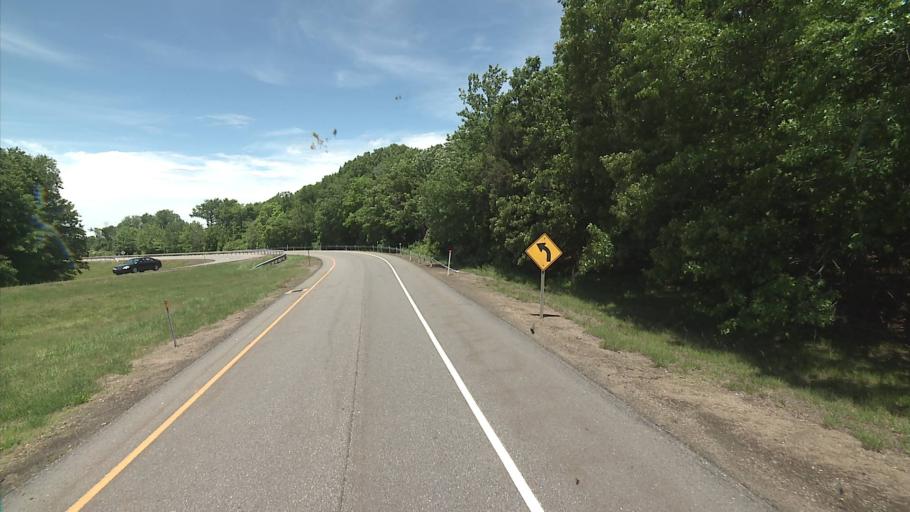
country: US
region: Connecticut
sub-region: New Haven County
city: Madison
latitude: 41.2913
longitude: -72.5672
